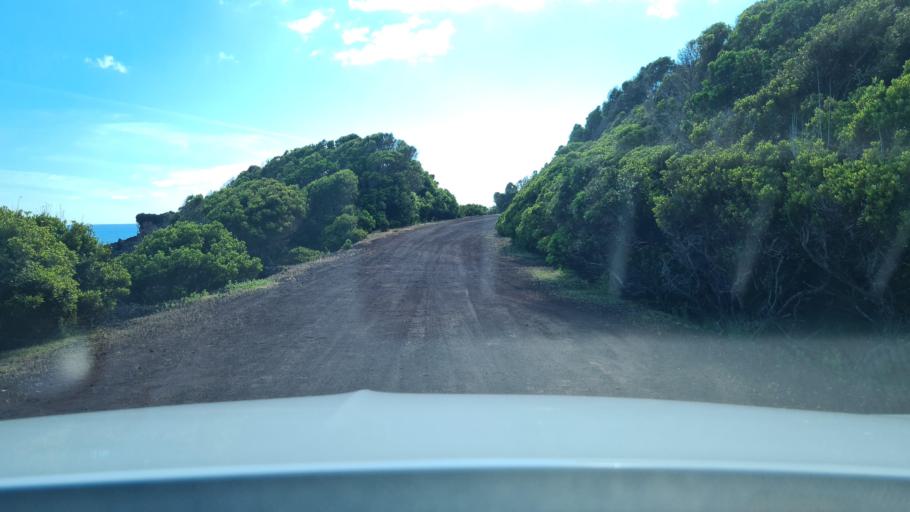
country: PT
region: Azores
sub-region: Sao Roque do Pico
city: Sao Roque do Pico
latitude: 38.4115
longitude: -28.3053
